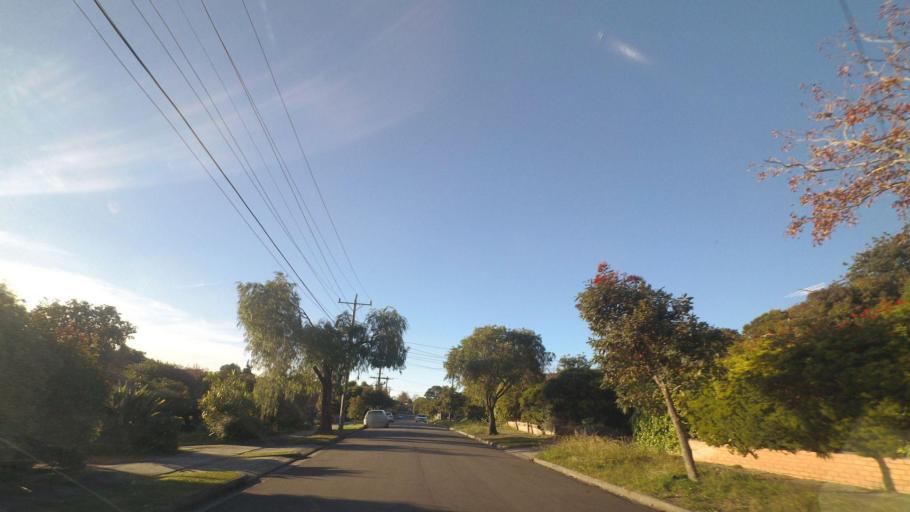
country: AU
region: Victoria
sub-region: Manningham
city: Doncaster East
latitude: -37.7946
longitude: 145.1540
